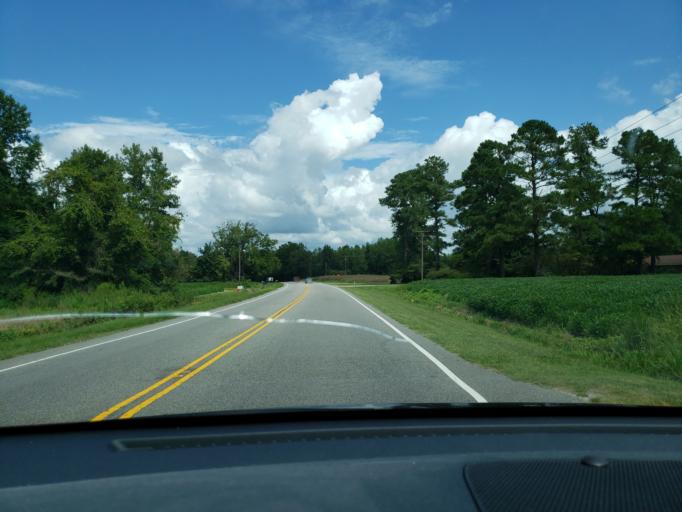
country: US
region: North Carolina
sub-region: Columbus County
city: Brunswick
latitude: 34.2307
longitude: -78.7532
